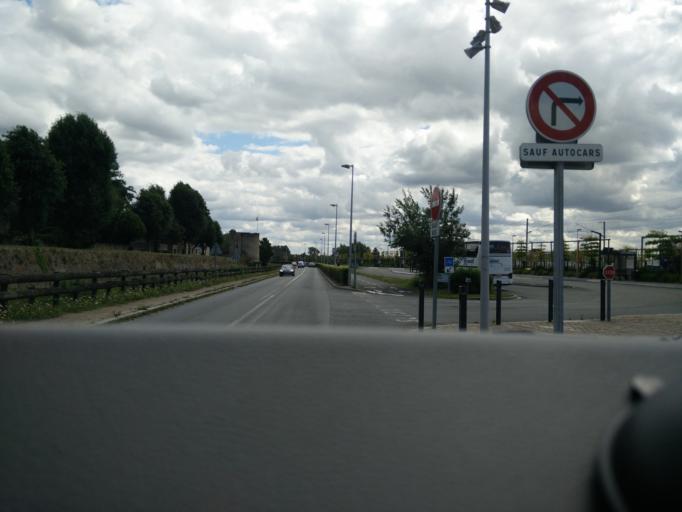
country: FR
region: Nord-Pas-de-Calais
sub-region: Departement du Nord
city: Bergues
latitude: 50.9690
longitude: 2.4262
